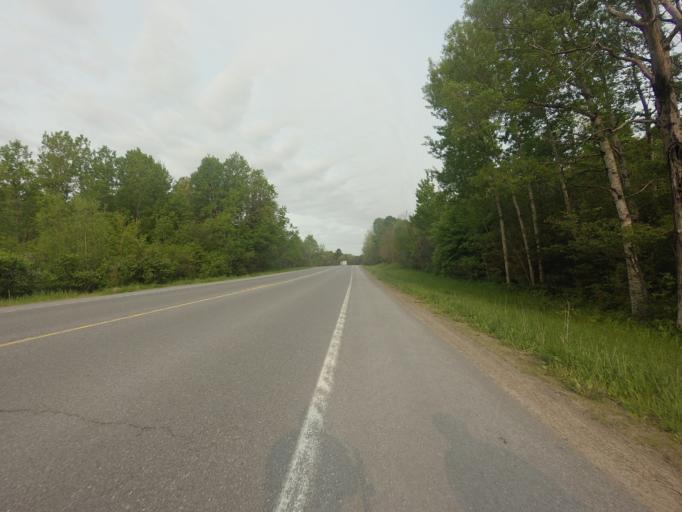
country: US
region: New York
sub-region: Jefferson County
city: Carthage
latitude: 44.0342
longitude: -75.6133
